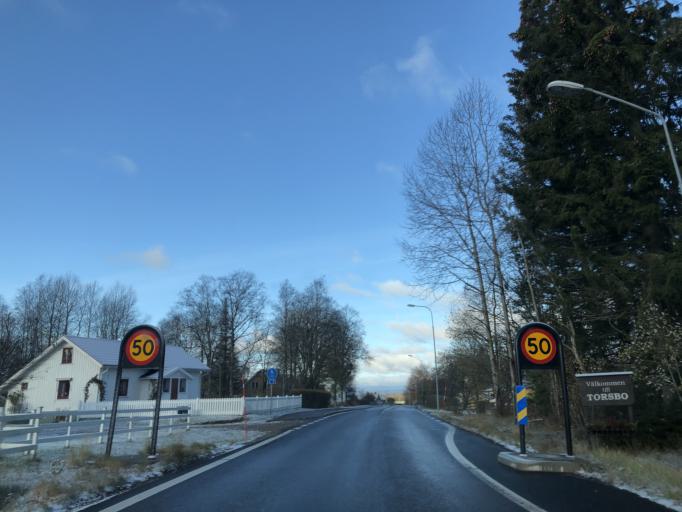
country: SE
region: Vaestra Goetaland
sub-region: Tranemo Kommun
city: Limmared
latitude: 57.6200
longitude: 13.4689
